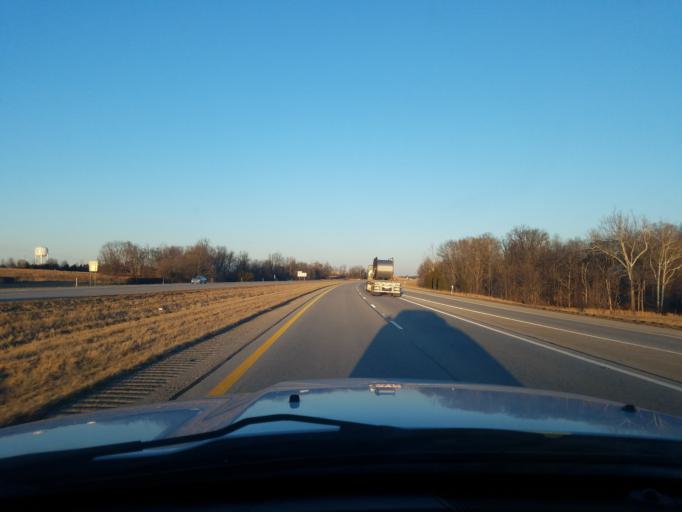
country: US
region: Indiana
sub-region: Floyd County
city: Georgetown
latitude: 38.2660
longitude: -85.9986
